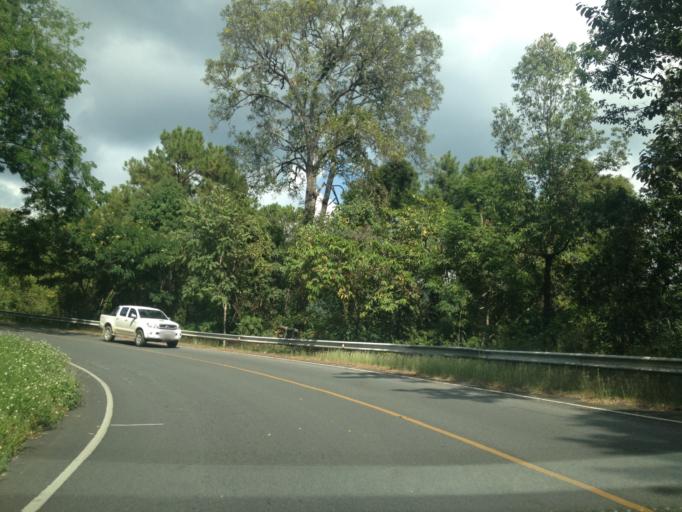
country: TH
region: Chiang Mai
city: Samoeng
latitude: 18.8334
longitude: 98.7836
